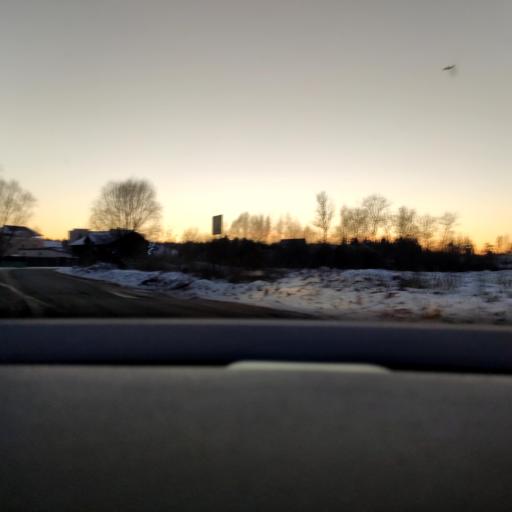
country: RU
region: Moskovskaya
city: Skhodnya
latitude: 55.8939
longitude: 37.3050
